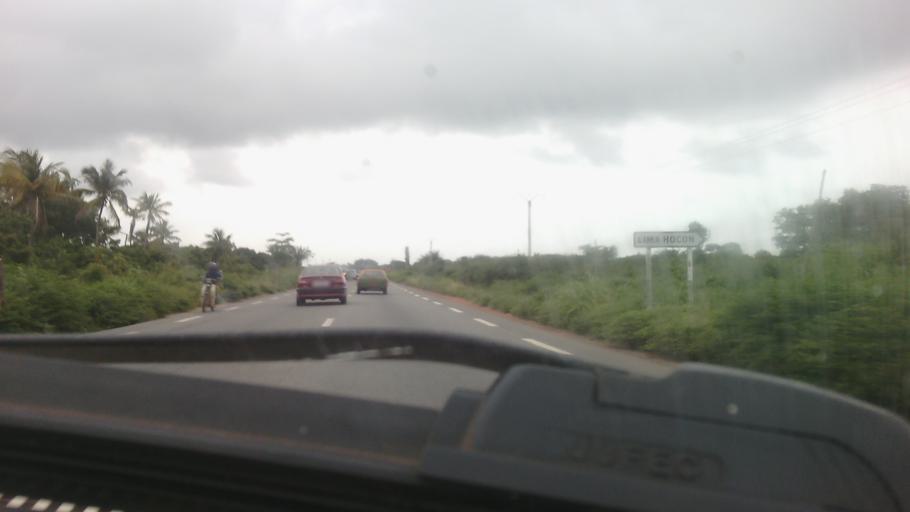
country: BJ
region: Atlantique
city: Ouidah
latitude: 6.3665
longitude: 2.0457
